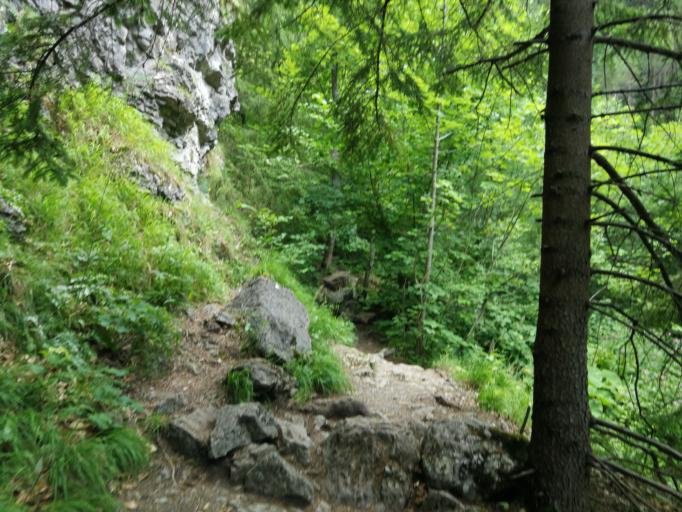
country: SK
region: Zilinsky
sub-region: Okres Liptovsky Mikulas
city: Liptovsky Mikulas
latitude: 49.1761
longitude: 19.4878
